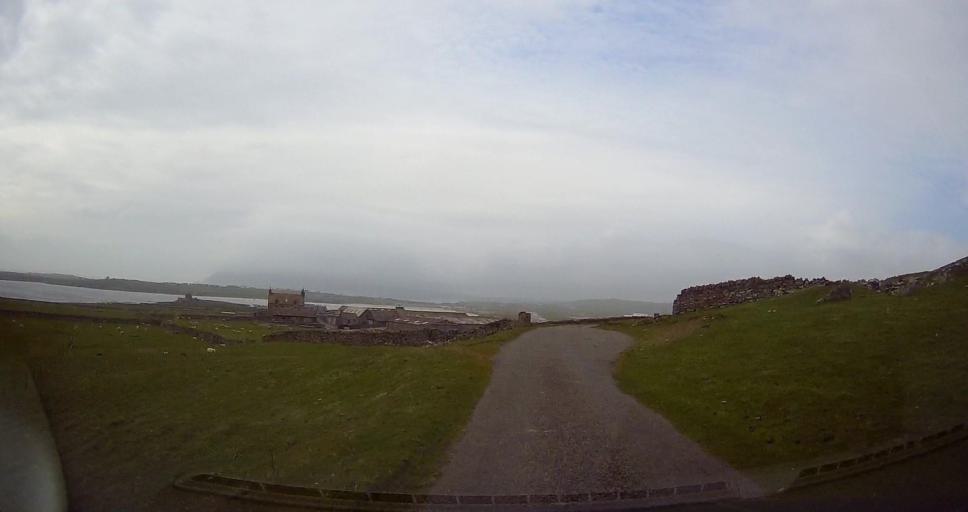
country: GB
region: Scotland
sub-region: Shetland Islands
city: Sandwick
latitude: 59.8662
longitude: -1.2782
